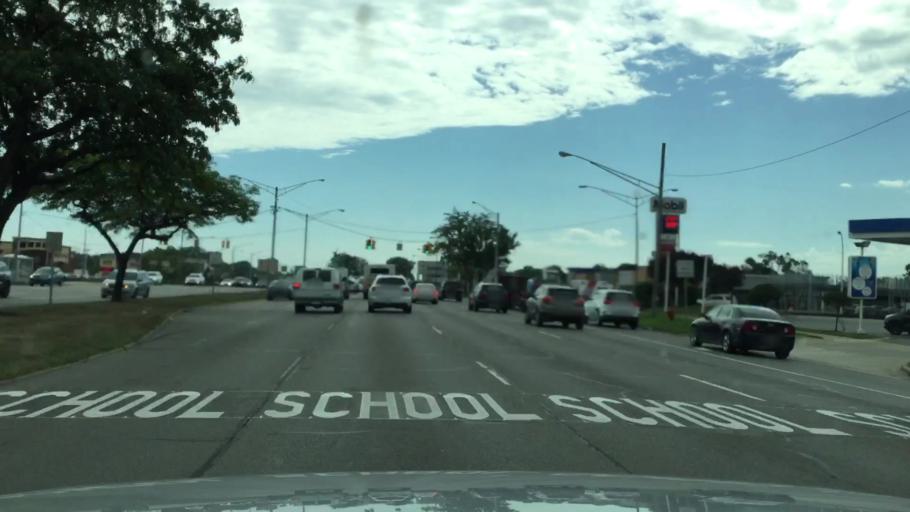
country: US
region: Michigan
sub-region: Oakland County
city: Berkley
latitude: 42.5187
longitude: -83.1872
